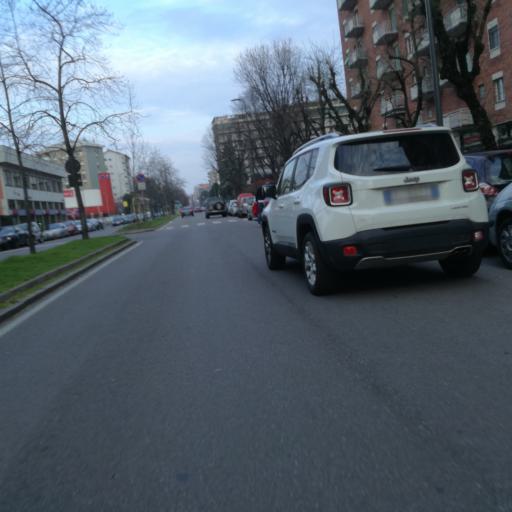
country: IT
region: Lombardy
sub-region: Citta metropolitana di Milano
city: Romano Banco
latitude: 45.4542
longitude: 9.1340
